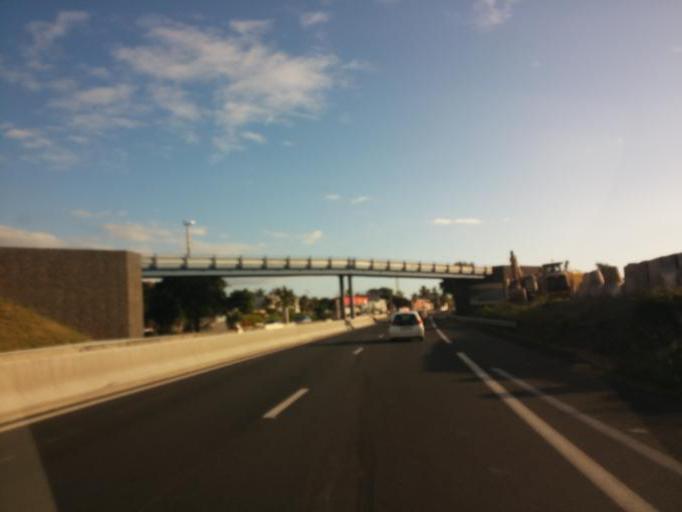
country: RE
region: Reunion
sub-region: Reunion
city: La Possession
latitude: -20.9225
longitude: 55.3445
